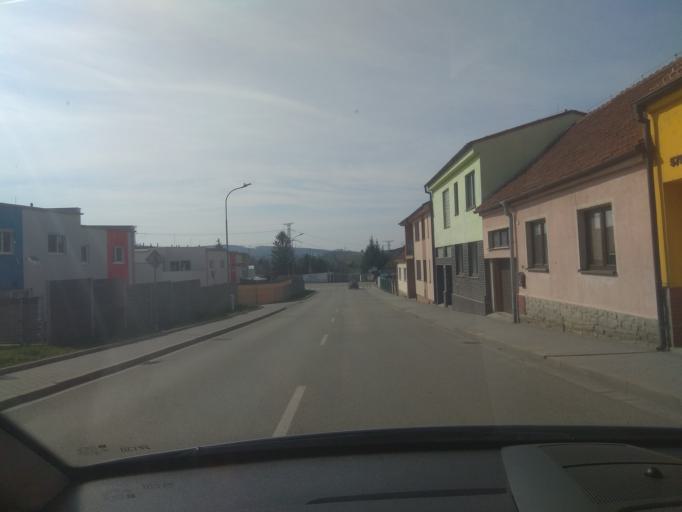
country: CZ
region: South Moravian
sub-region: Okres Brno-Venkov
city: Rosice
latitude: 49.1794
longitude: 16.3986
